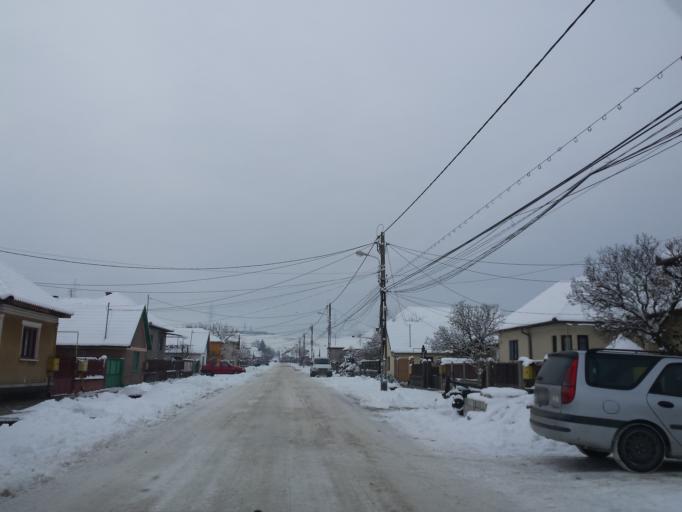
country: RO
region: Hunedoara
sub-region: Municipiul Deva
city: Cristur
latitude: 45.8232
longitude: 22.9312
